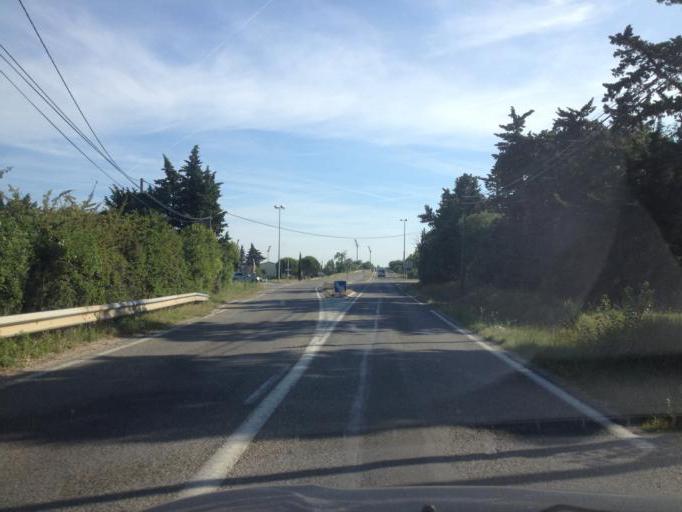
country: FR
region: Provence-Alpes-Cote d'Azur
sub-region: Departement du Vaucluse
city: Orange
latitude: 44.1195
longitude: 4.7976
